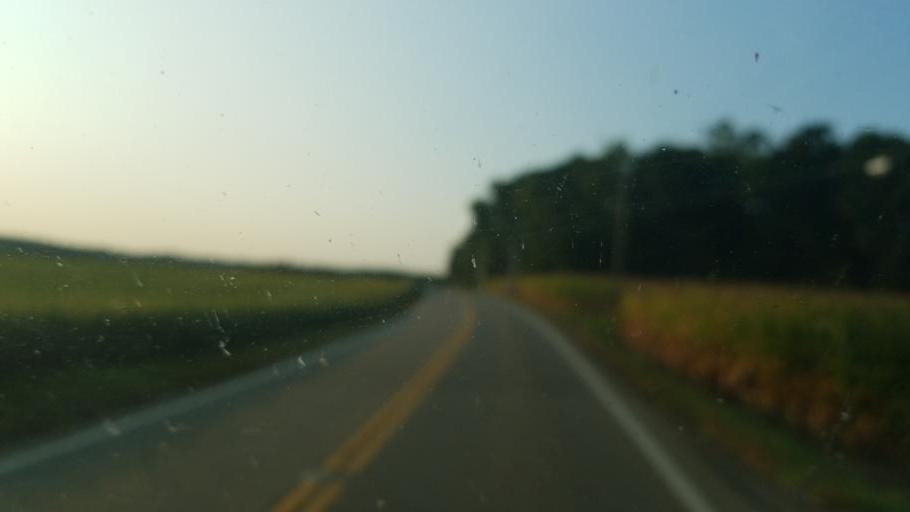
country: US
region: Ohio
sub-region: Ashland County
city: Loudonville
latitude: 40.6604
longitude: -82.1389
